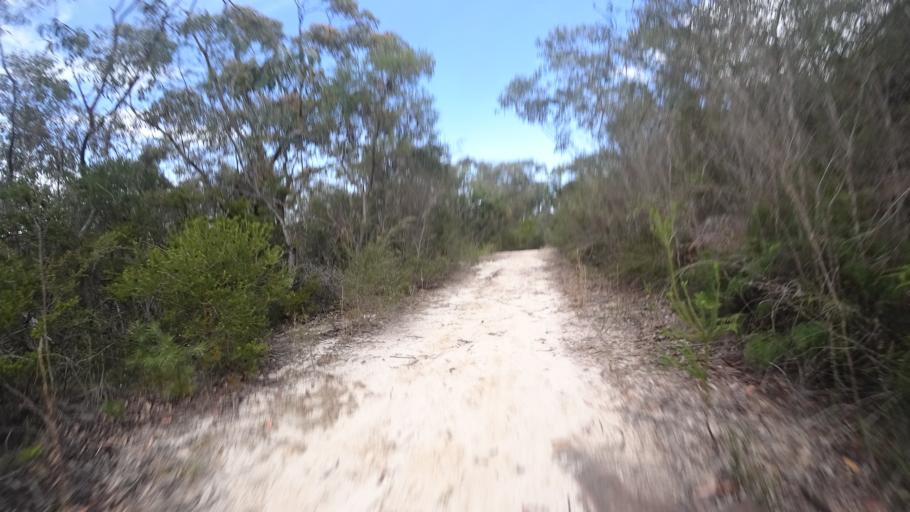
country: AU
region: New South Wales
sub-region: City of Sydney
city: North Turramurra
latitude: -33.6840
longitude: 151.1967
